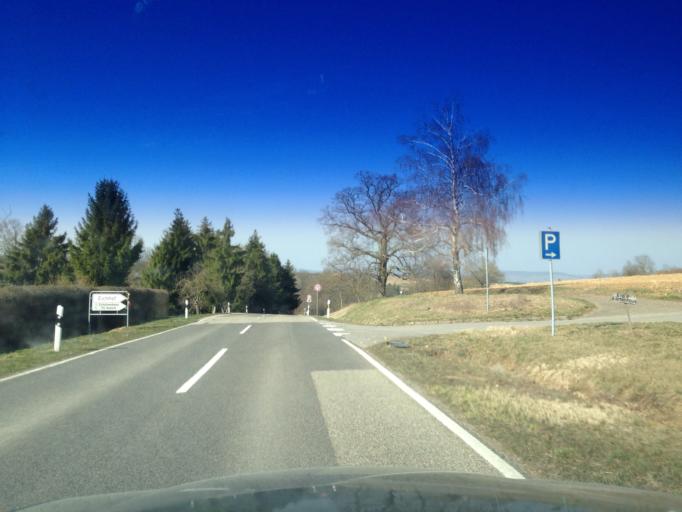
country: DE
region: Baden-Wuerttemberg
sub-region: Regierungsbezirk Stuttgart
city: Vaihingen an der Enz
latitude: 48.9070
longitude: 8.9393
